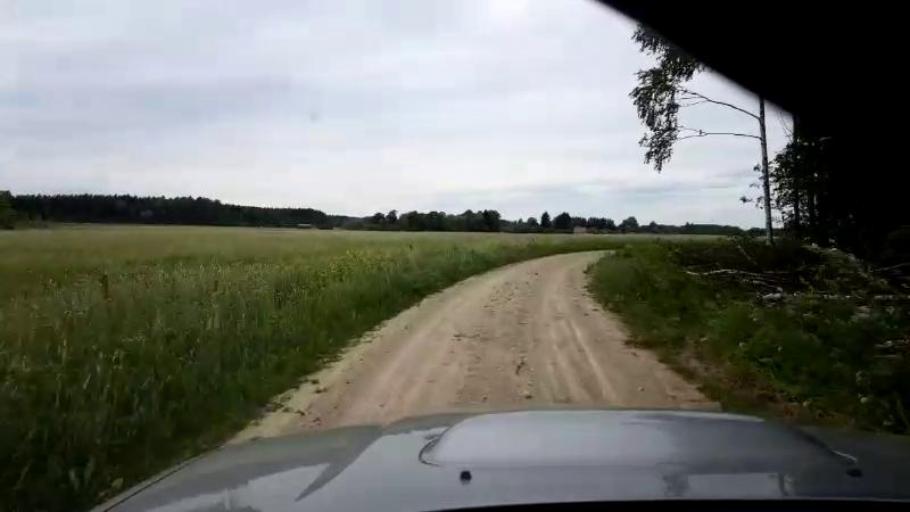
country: EE
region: Paernumaa
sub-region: Sindi linn
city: Sindi
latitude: 58.5125
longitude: 24.6200
